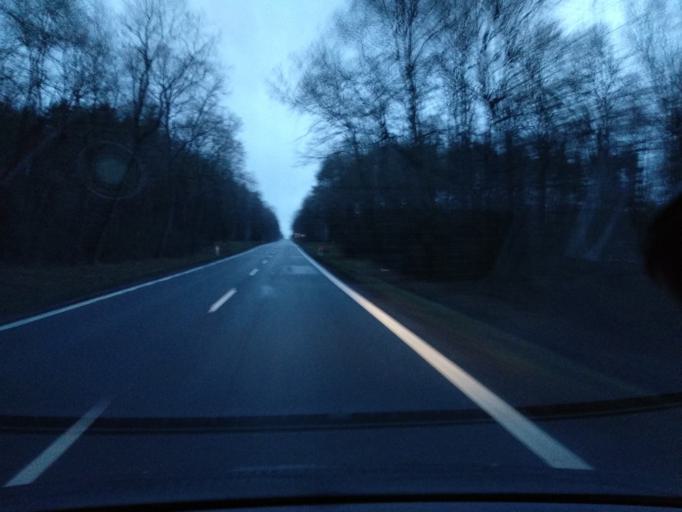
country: PL
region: Lower Silesian Voivodeship
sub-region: Powiat legnicki
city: Prochowice
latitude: 51.2457
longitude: 16.4085
